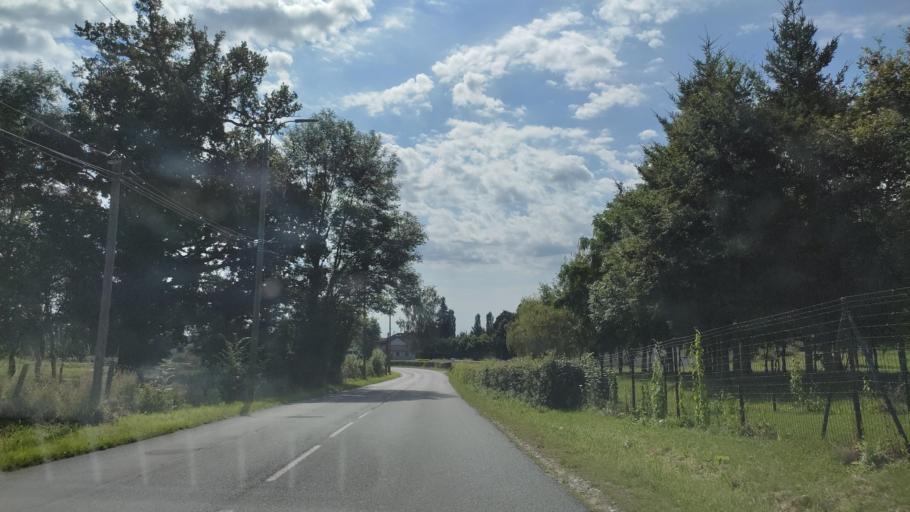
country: FR
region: Limousin
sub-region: Departement de la Haute-Vienne
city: Isle
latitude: 45.8337
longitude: 1.1951
